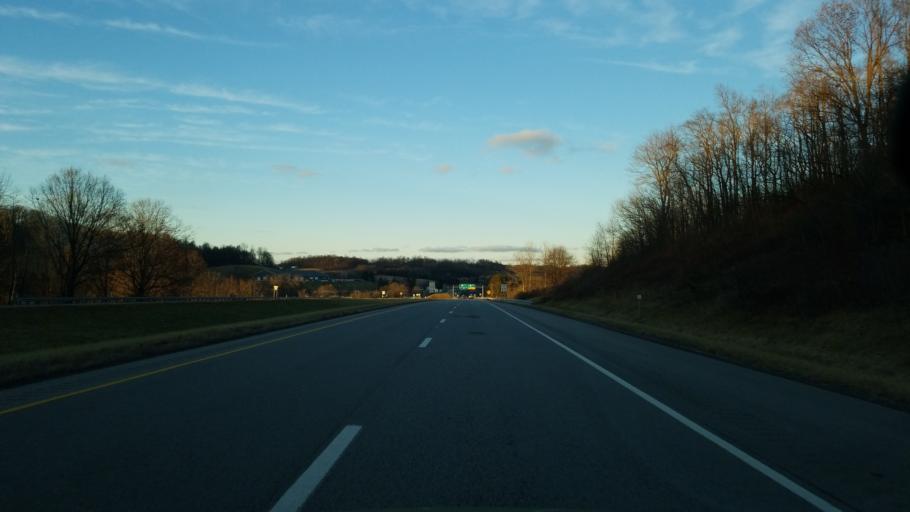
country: US
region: Pennsylvania
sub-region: Indiana County
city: Chevy Chase Heights
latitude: 40.6632
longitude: -79.1139
